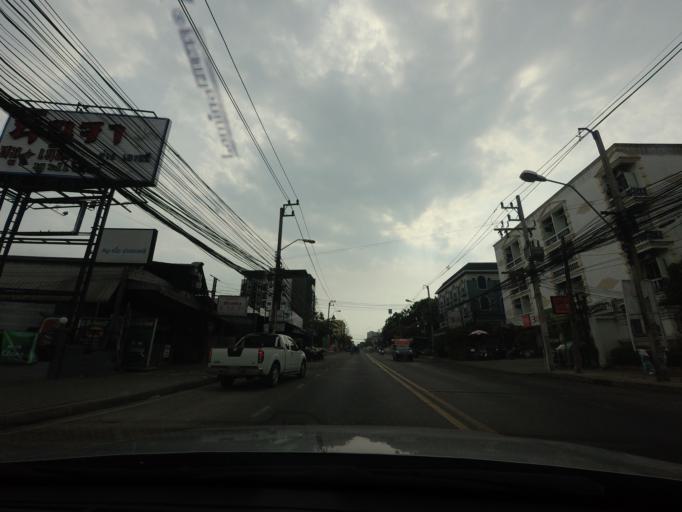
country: TH
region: Chon Buri
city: Phatthaya
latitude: 12.9667
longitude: 100.8990
